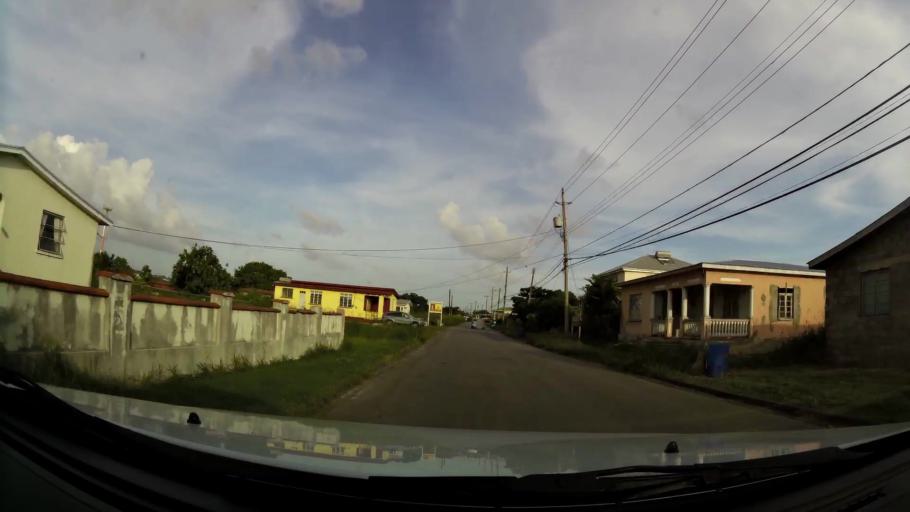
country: BB
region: Christ Church
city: Oistins
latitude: 13.0580
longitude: -59.5209
